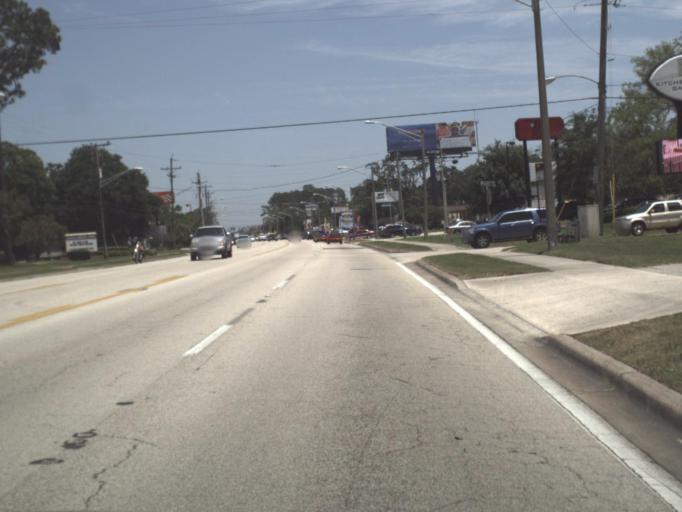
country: US
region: Florida
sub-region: Duval County
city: Jacksonville
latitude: 30.2908
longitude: -81.5962
